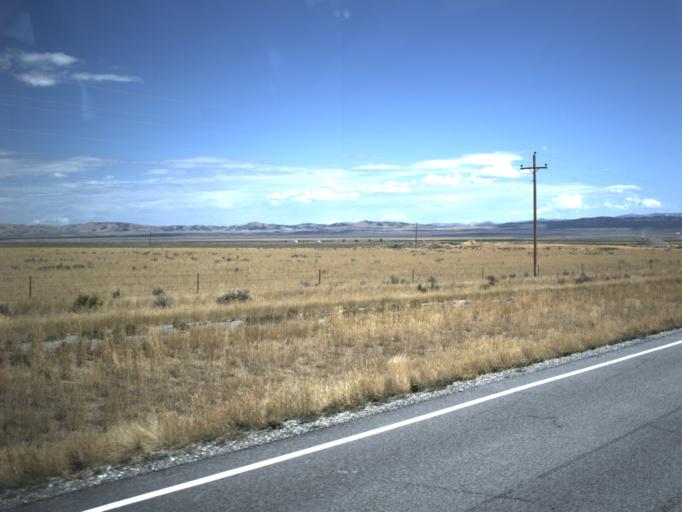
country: US
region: Idaho
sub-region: Oneida County
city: Malad City
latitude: 41.9659
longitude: -112.9837
